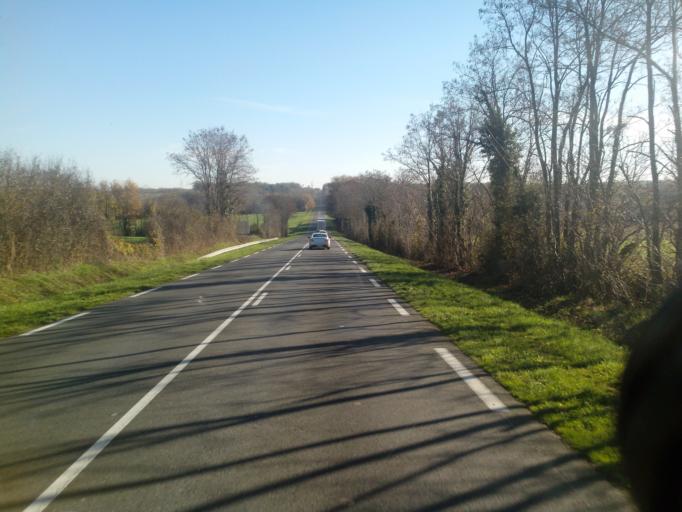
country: FR
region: Poitou-Charentes
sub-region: Departement de la Vienne
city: Terce
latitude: 46.4309
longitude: 0.6104
